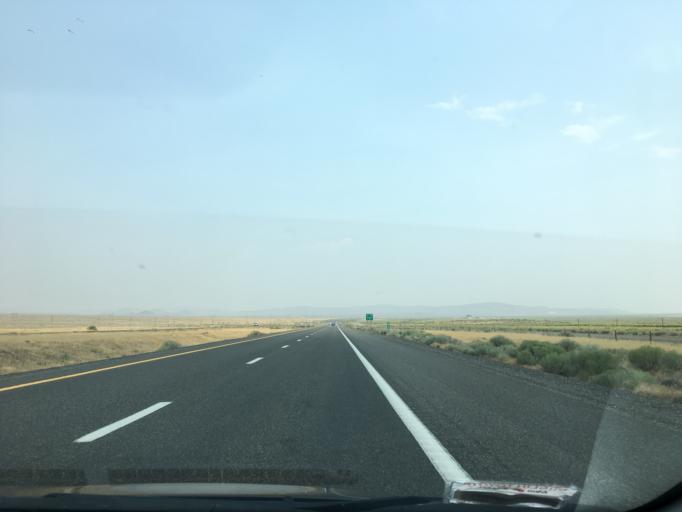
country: US
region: Nevada
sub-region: Pershing County
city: Lovelock
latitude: 40.0434
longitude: -118.6626
